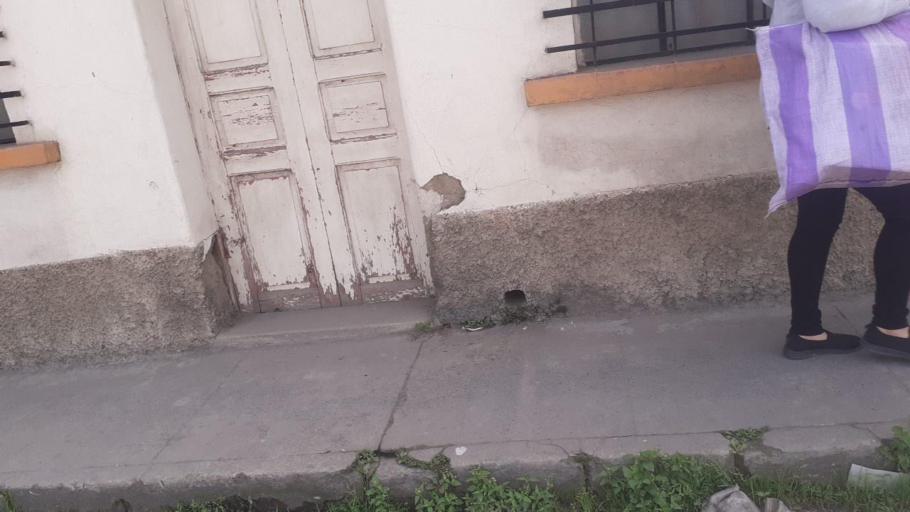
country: GT
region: Quetzaltenango
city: Quetzaltenango
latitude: 14.8353
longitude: -91.5258
